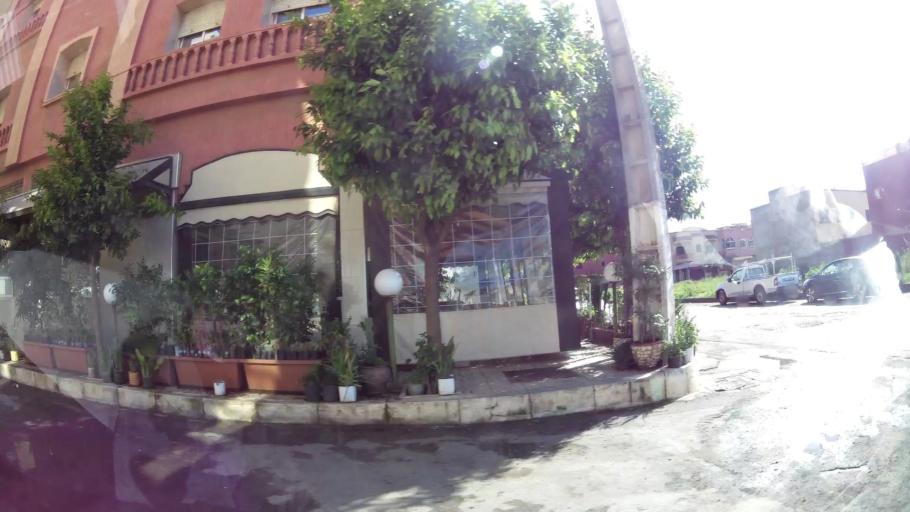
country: MA
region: Grand Casablanca
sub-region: Mediouna
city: Mediouna
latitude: 33.3845
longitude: -7.5357
